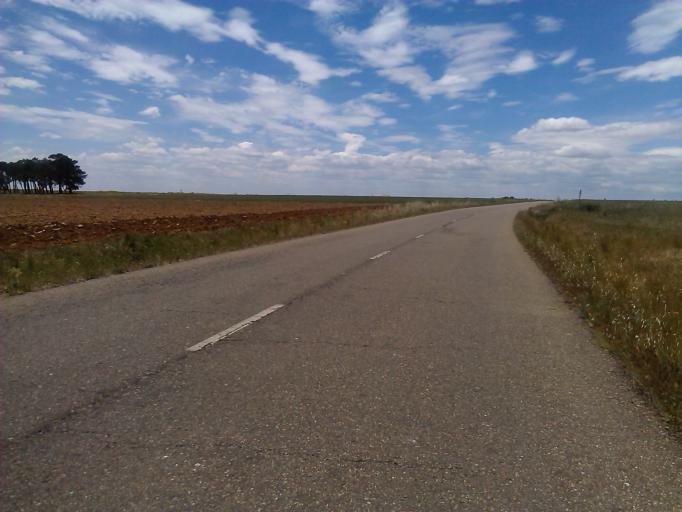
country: ES
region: Castille and Leon
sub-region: Provincia de Leon
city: Chozas de Abajo
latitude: 42.4905
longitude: -5.7134
